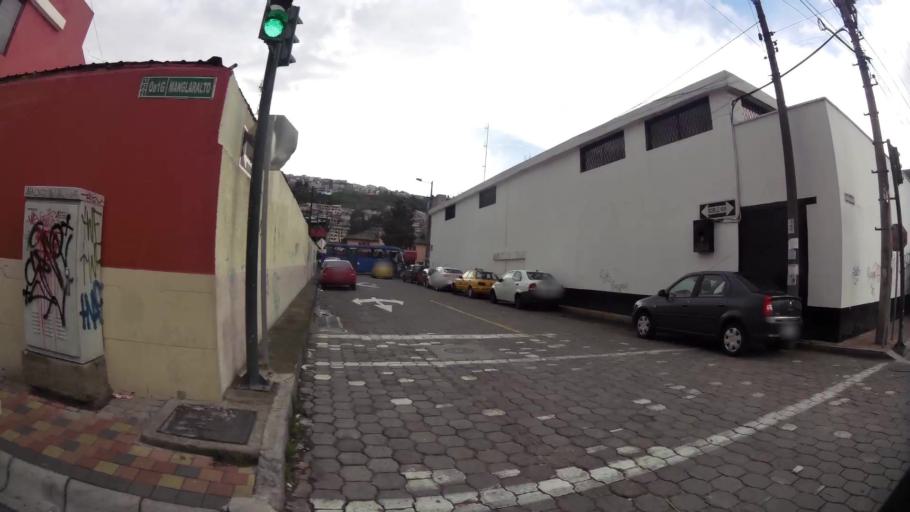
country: EC
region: Pichincha
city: Quito
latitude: -0.2852
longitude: -78.5372
